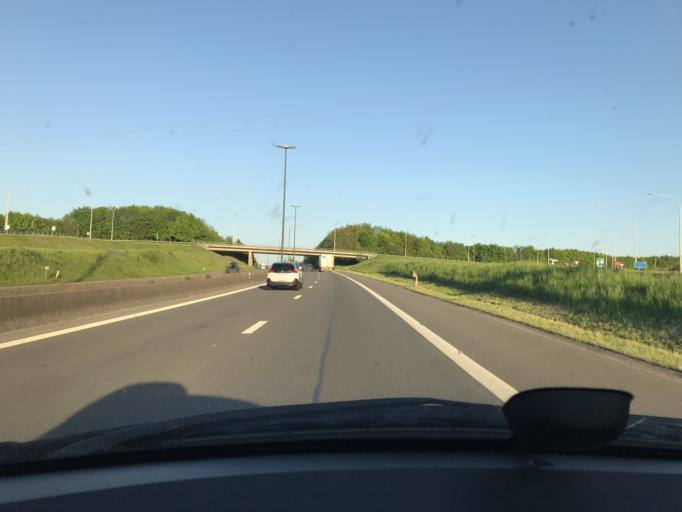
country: BE
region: Wallonia
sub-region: Province du Luxembourg
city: Wellin
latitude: 50.0949
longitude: 5.1329
